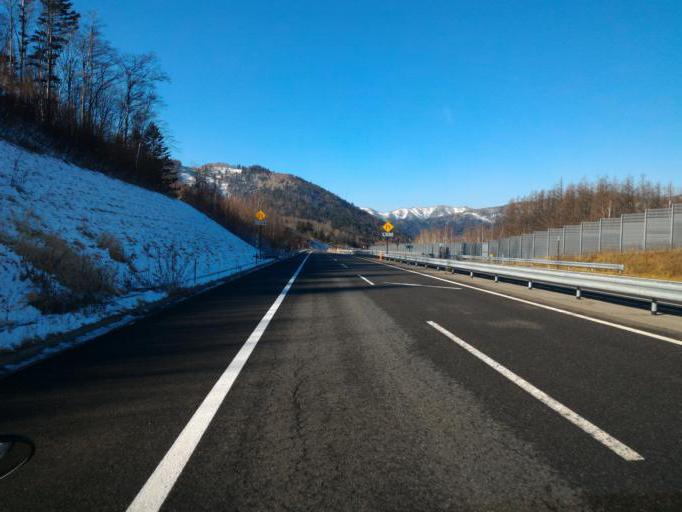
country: JP
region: Hokkaido
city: Shimo-furano
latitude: 43.0545
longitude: 142.5725
